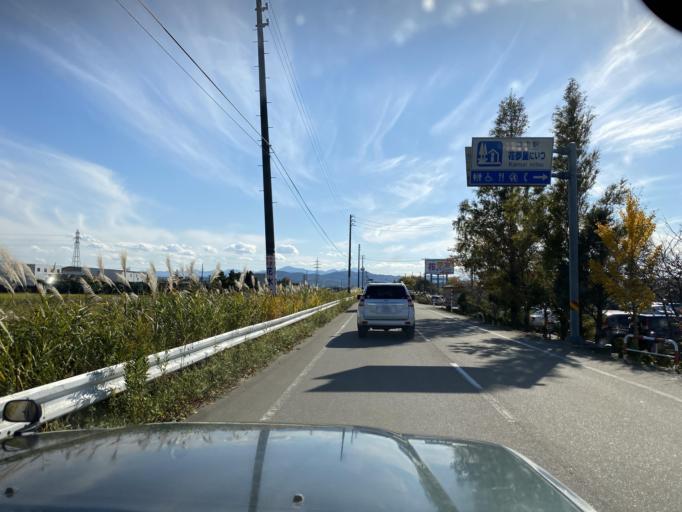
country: JP
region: Niigata
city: Niitsu-honcho
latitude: 37.7934
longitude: 139.0792
